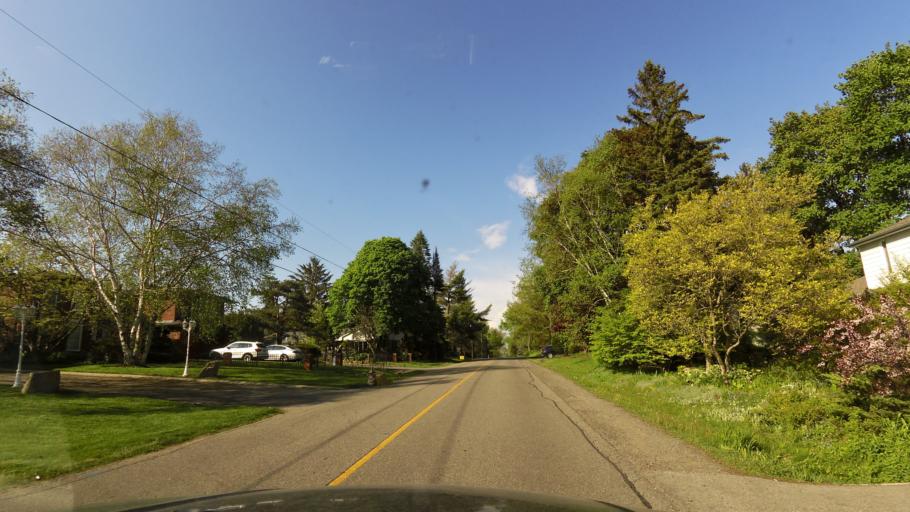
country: CA
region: Ontario
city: Mississauga
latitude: 43.5624
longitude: -79.6039
